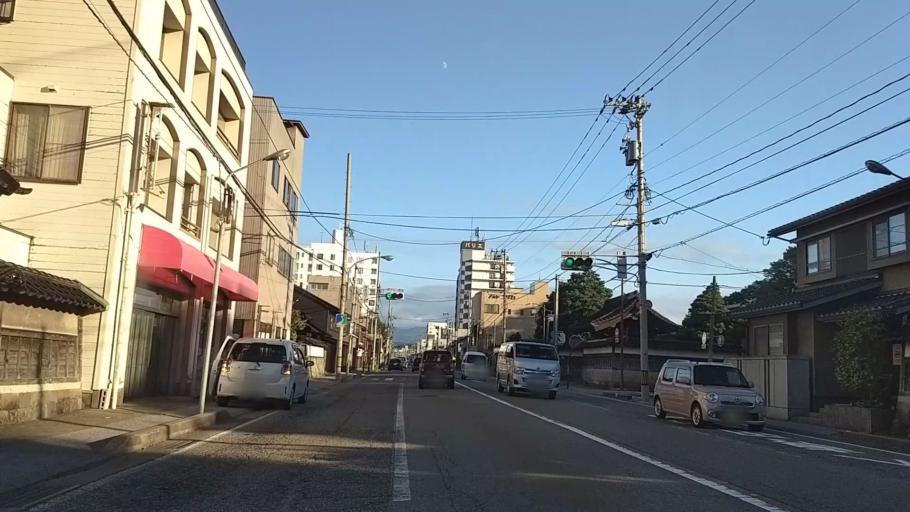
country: JP
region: Ishikawa
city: Nonoichi
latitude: 36.5526
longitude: 136.6536
